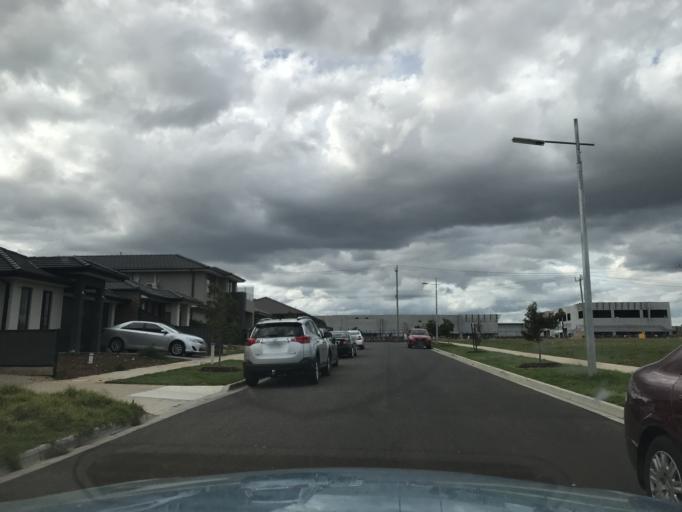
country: AU
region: Victoria
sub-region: Wyndham
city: Williams Landing
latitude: -37.8402
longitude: 144.7439
